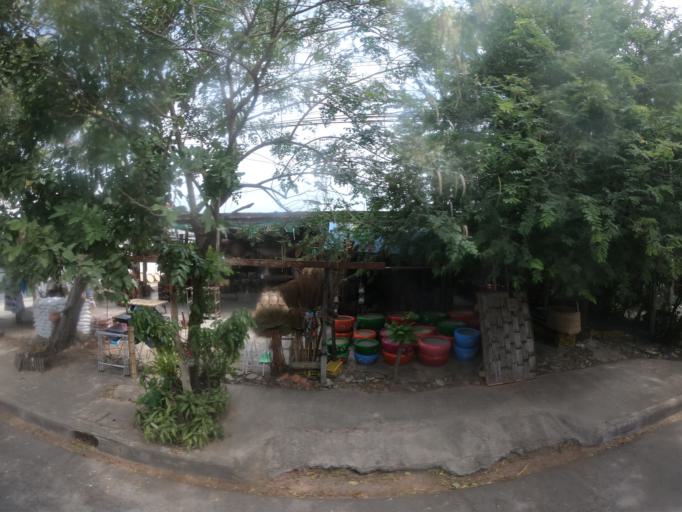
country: TH
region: Maha Sarakham
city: Chiang Yuen
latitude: 16.4050
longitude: 103.0989
